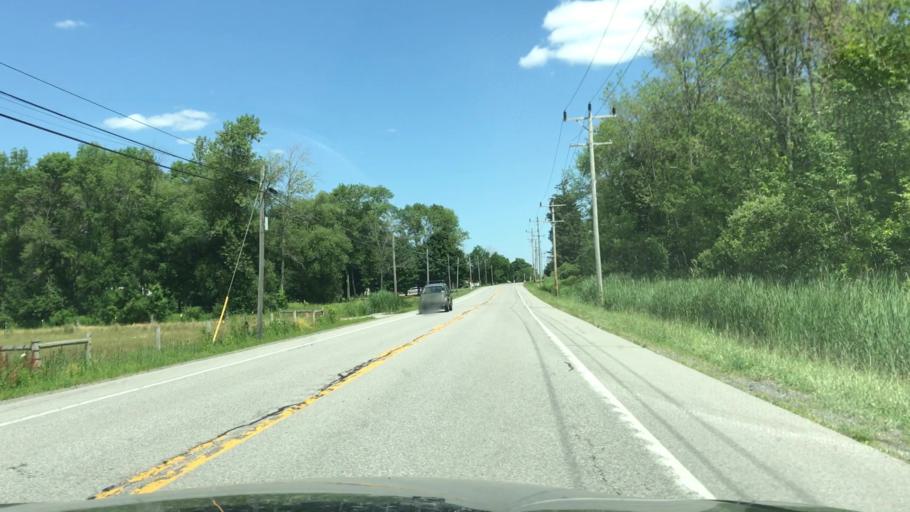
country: US
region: New York
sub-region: Wyoming County
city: Warsaw
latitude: 42.7440
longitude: -78.0697
